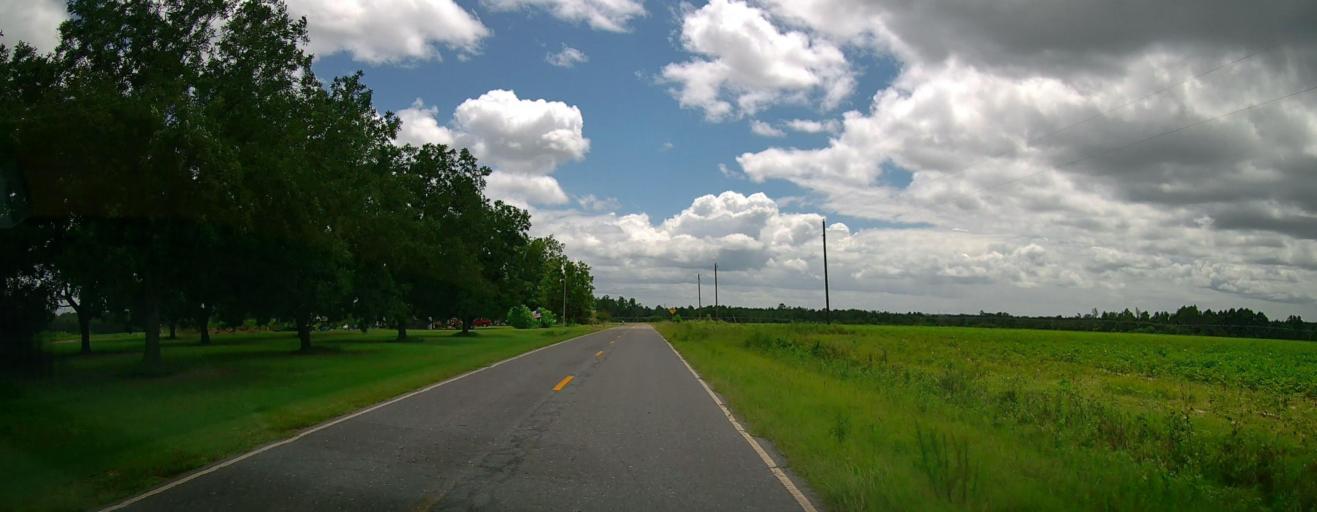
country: US
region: Georgia
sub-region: Ben Hill County
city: Fitzgerald
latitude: 31.6545
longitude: -83.4012
